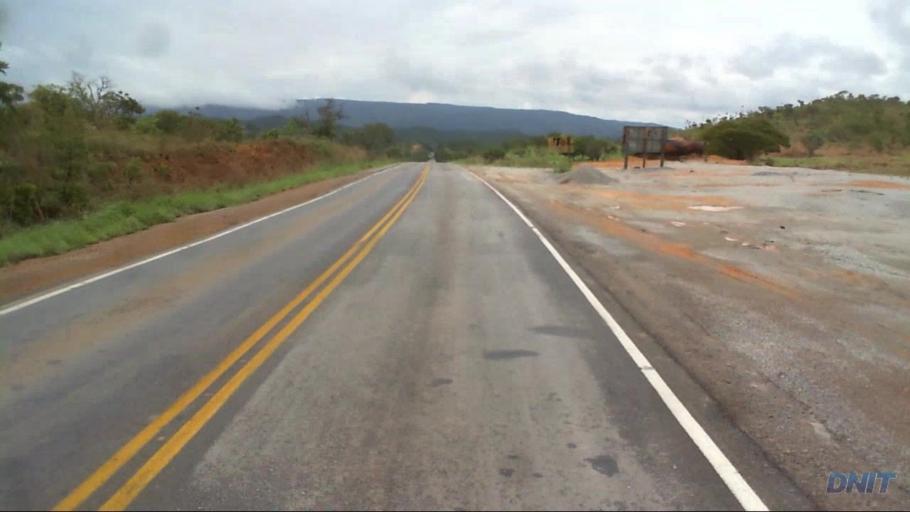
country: BR
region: Goias
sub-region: Padre Bernardo
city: Padre Bernardo
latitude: -15.4673
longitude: -48.2279
